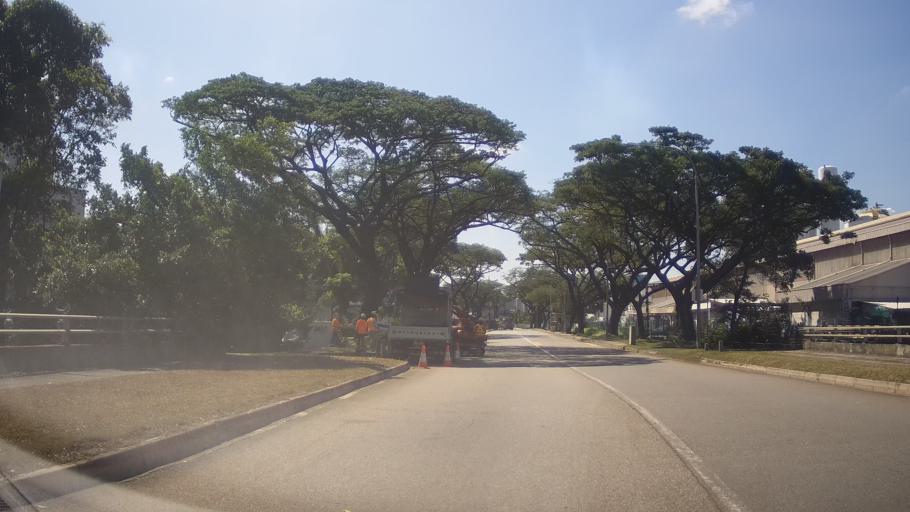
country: SG
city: Singapore
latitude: 1.3088
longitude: 103.6983
